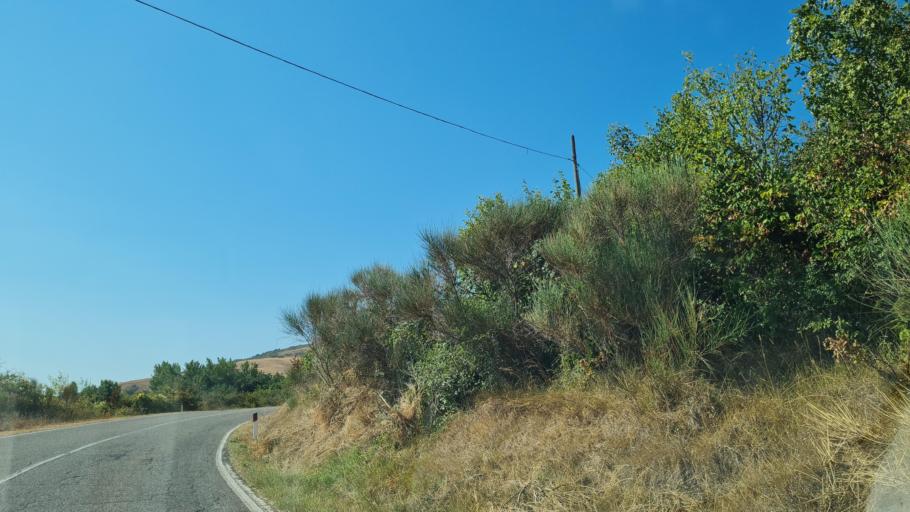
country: IT
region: Tuscany
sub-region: Provincia di Siena
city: Abbadia San Salvatore
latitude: 42.9388
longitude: 11.7118
